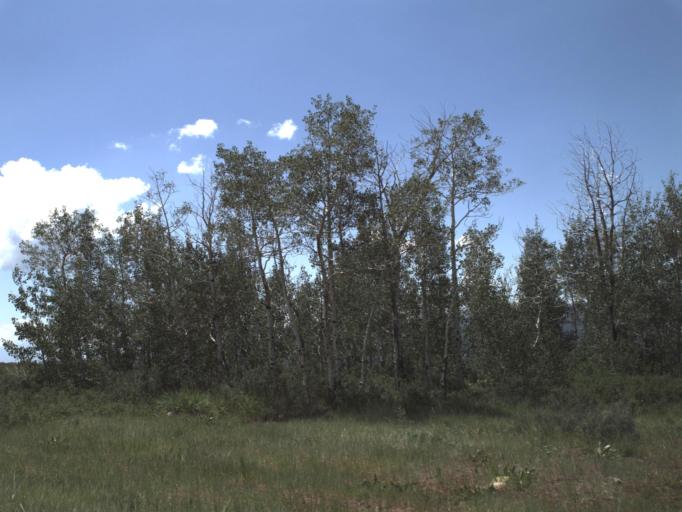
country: US
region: Utah
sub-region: Weber County
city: Wolf Creek
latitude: 41.4149
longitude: -111.5586
